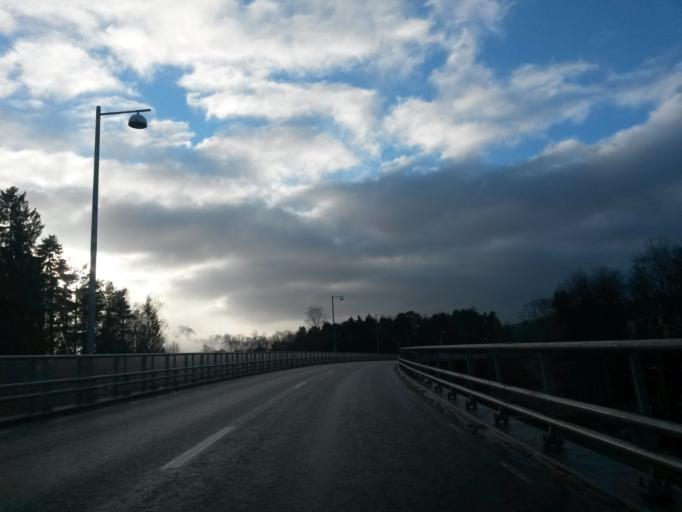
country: SE
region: Vaestra Goetaland
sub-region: Boras Kommun
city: Boras
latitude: 57.7442
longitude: 12.9460
